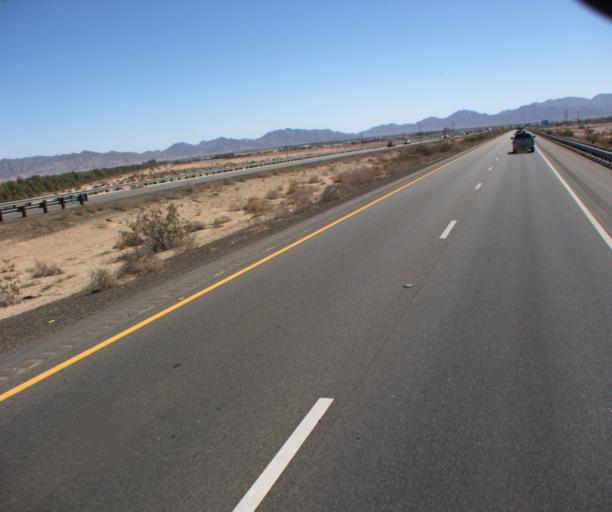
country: US
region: Arizona
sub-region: Yuma County
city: Fortuna Foothills
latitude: 32.6772
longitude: -114.5022
